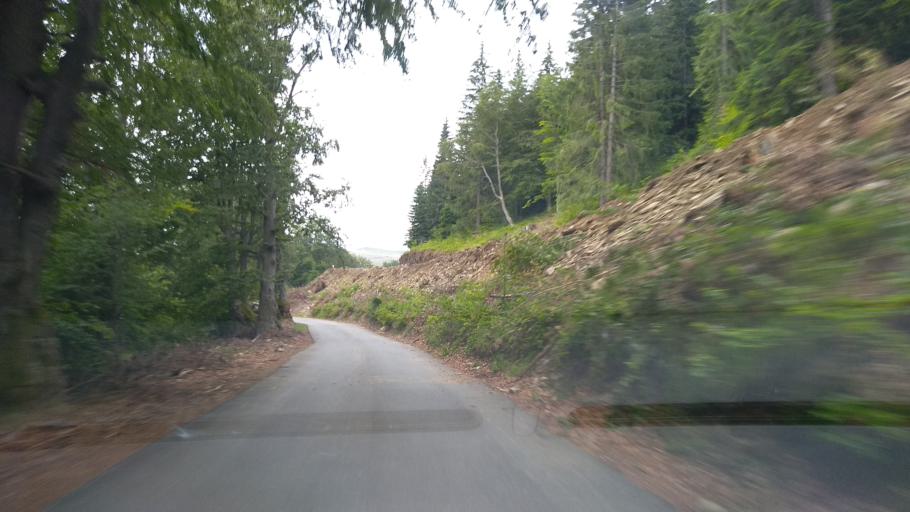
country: RO
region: Hunedoara
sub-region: Municipiul  Vulcan
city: Jiu-Paroseni
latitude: 45.3235
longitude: 23.2925
